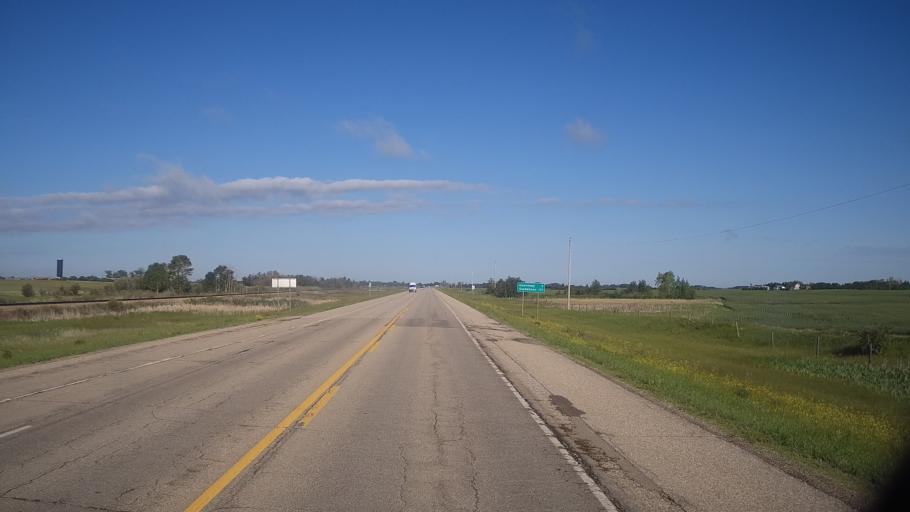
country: CA
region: Saskatchewan
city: Lanigan
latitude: 51.8668
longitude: -105.1486
